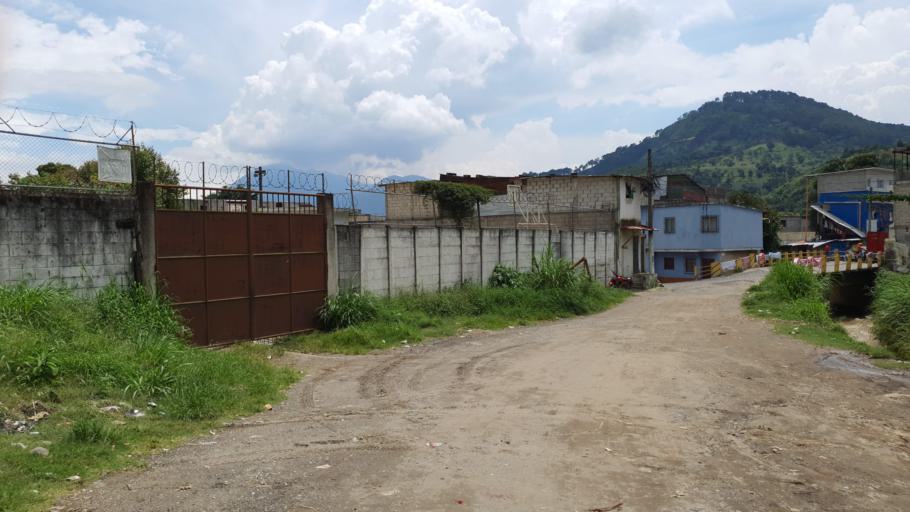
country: GT
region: Guatemala
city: Villa Canales
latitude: 14.4854
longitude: -90.5318
